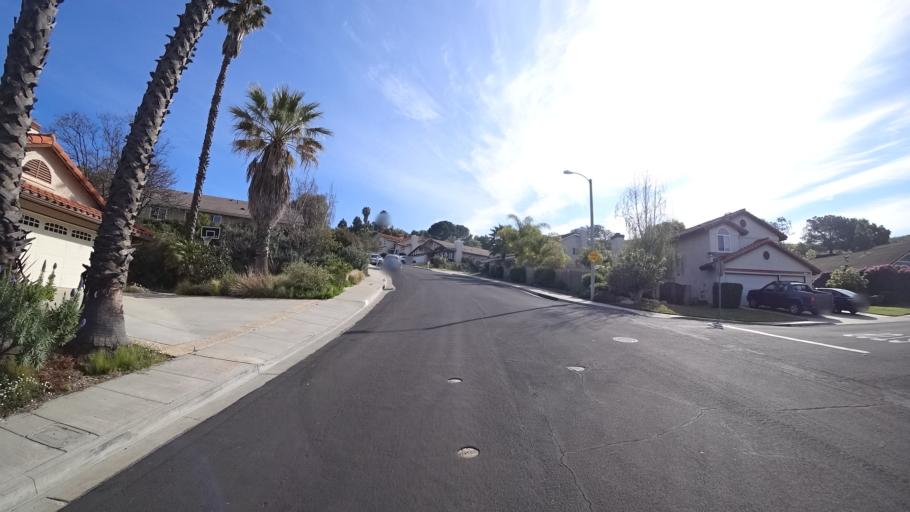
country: US
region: California
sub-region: Ventura County
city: Thousand Oaks
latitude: 34.2197
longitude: -118.8289
